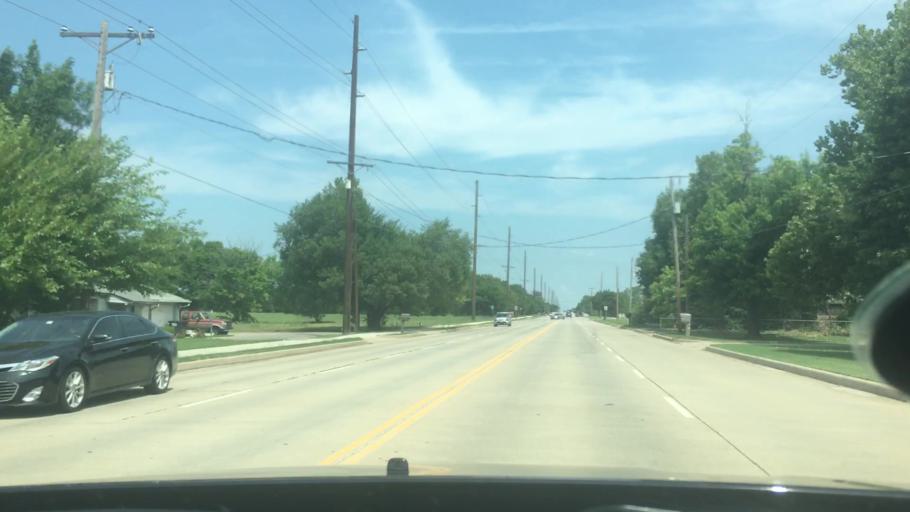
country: US
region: Oklahoma
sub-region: Pottawatomie County
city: Shawnee
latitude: 35.3506
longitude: -96.8942
